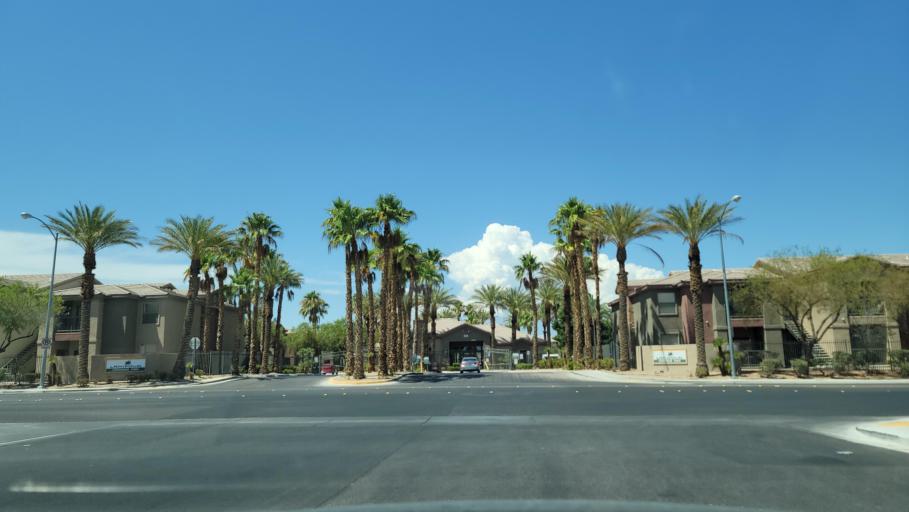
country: US
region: Nevada
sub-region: Clark County
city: Enterprise
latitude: 36.0609
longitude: -115.2655
